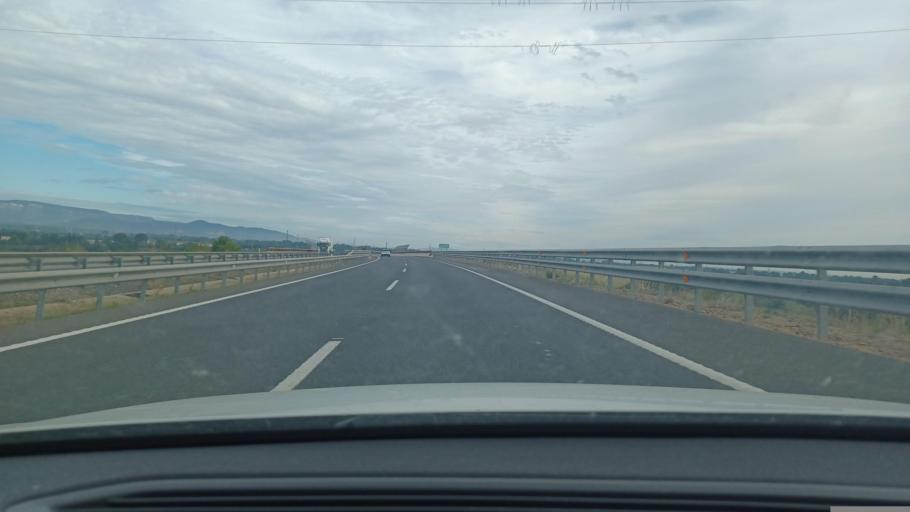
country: ES
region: Catalonia
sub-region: Provincia de Tarragona
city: Cambrils
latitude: 41.0688
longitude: 1.0112
